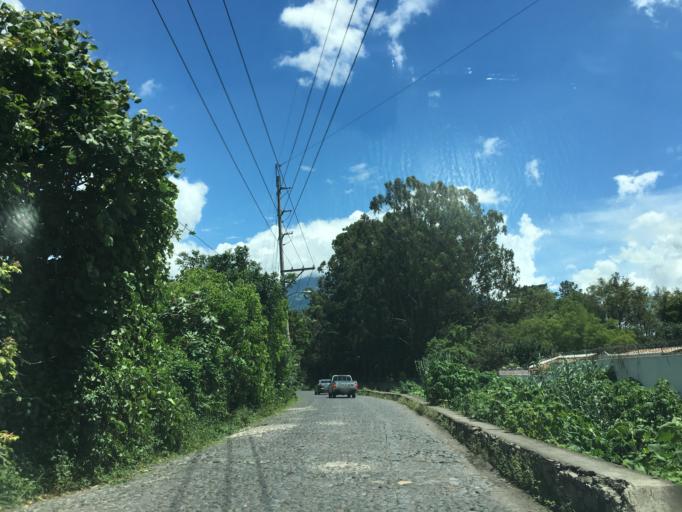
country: GT
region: Sacatepequez
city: Antigua Guatemala
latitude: 14.5539
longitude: -90.7273
